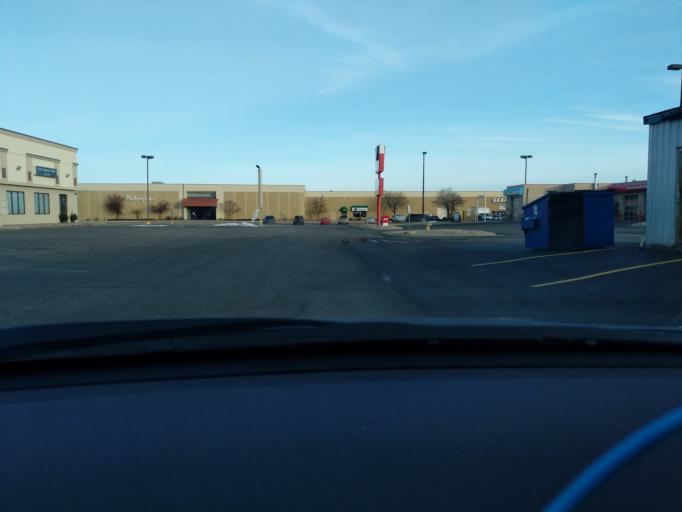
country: US
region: Minnesota
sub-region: Kandiyohi County
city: Willmar
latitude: 45.1075
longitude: -95.0420
